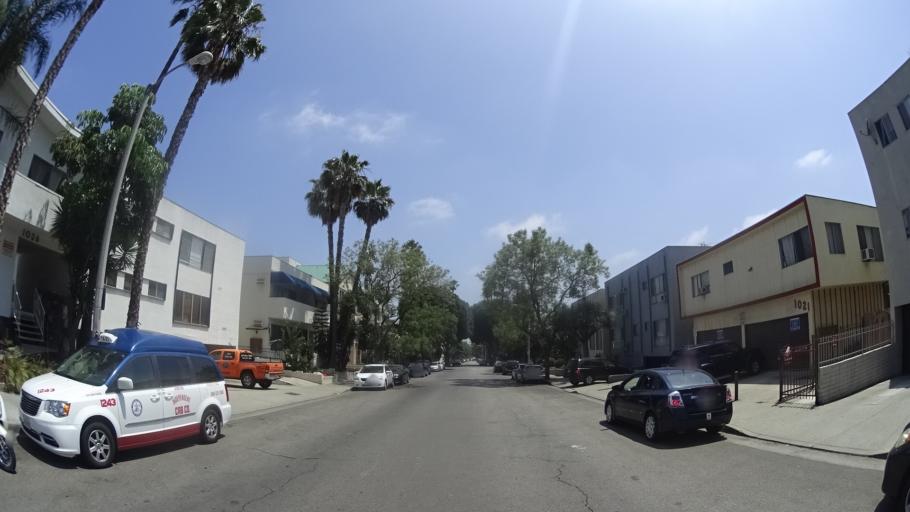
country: US
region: California
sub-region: Los Angeles County
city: West Hollywood
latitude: 34.0896
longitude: -118.3553
